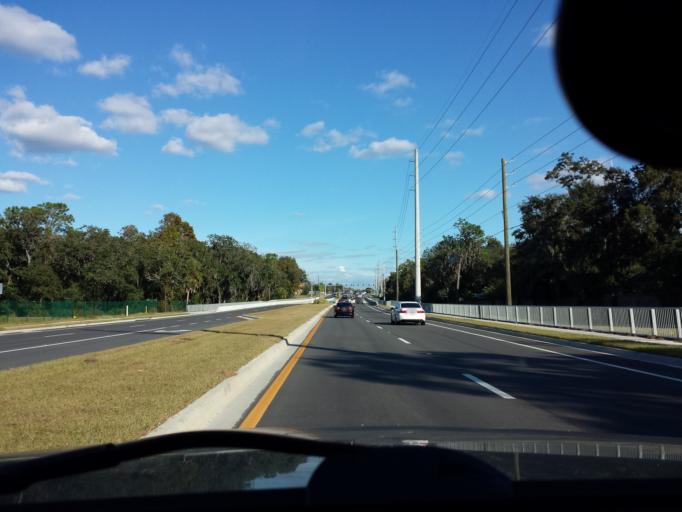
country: US
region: Florida
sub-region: Hillsborough County
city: Riverview
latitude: 27.8535
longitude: -82.2768
